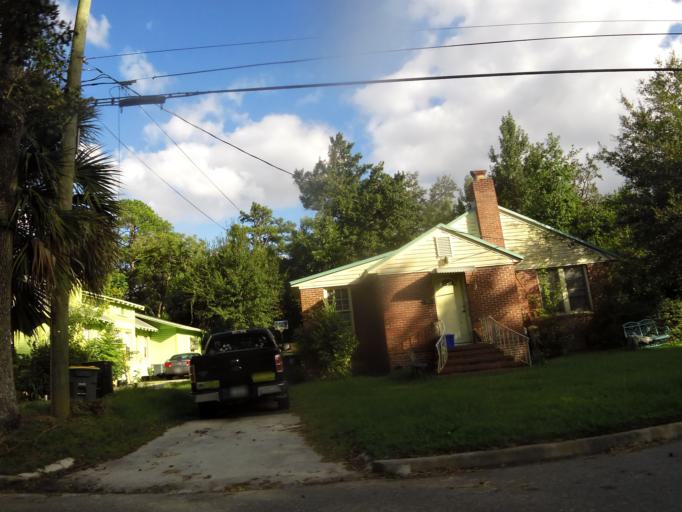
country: US
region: Florida
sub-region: Duval County
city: Jacksonville
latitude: 30.3108
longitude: -81.7131
